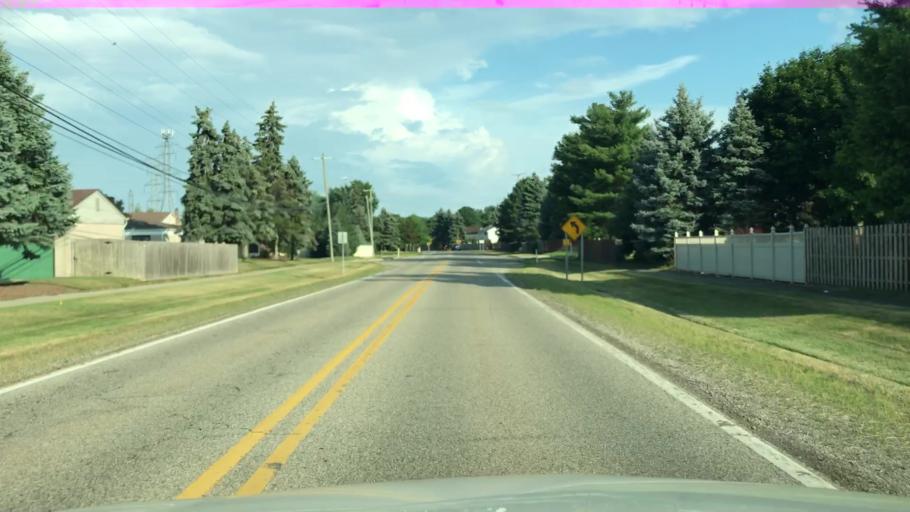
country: US
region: Michigan
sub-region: Macomb County
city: Sterling Heights
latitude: 42.5916
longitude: -82.9992
